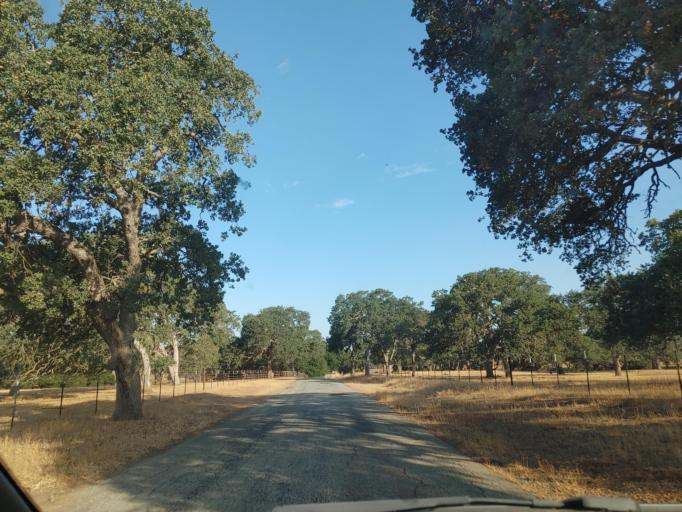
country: US
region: California
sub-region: San Benito County
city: Ridgemark
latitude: 36.7766
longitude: -121.2400
